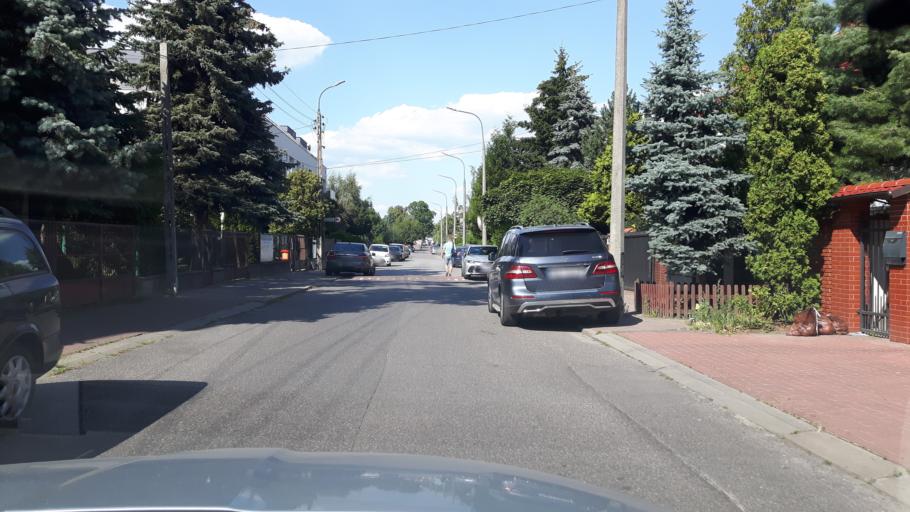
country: PL
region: Masovian Voivodeship
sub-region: Warszawa
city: Wlochy
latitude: 52.2004
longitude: 20.9197
